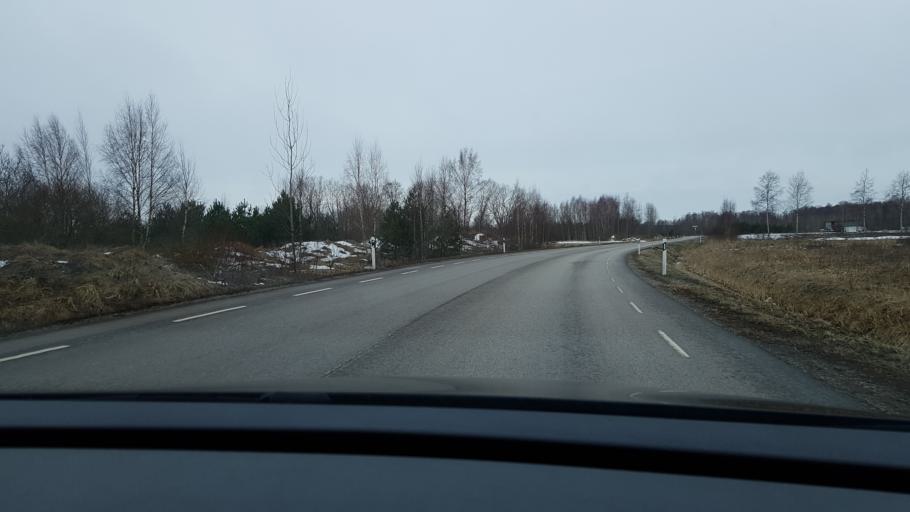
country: EE
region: Paernumaa
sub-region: Sauga vald
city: Sauga
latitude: 58.4092
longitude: 24.4377
